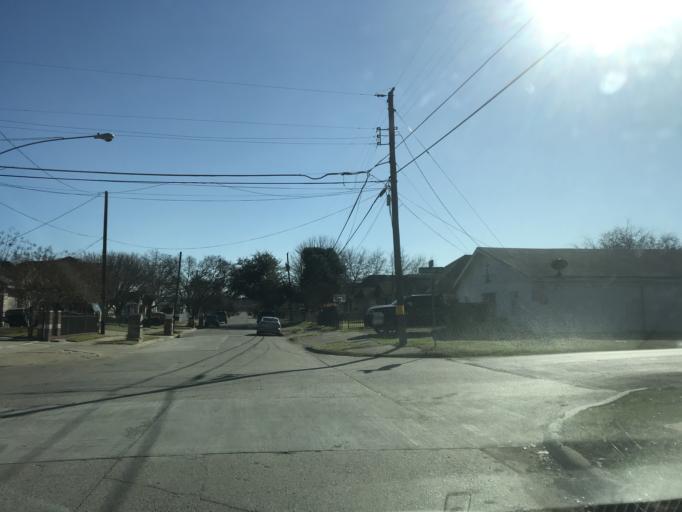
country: US
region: Texas
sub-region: Dallas County
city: Cockrell Hill
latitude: 32.7756
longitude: -96.9095
